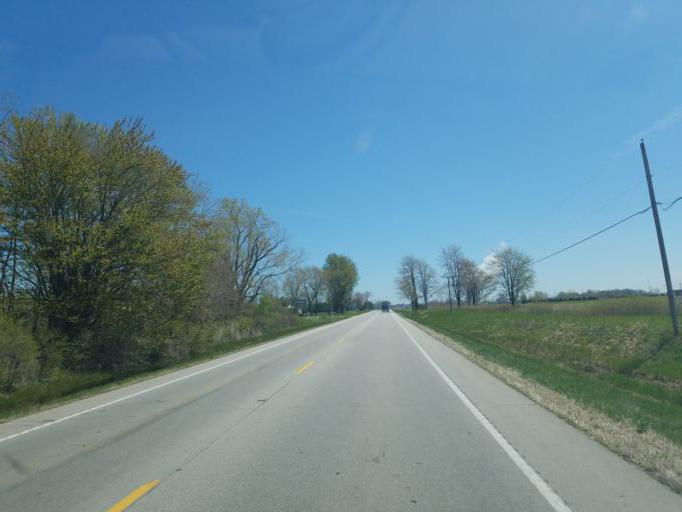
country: US
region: Ohio
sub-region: Ottawa County
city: Oak Harbor
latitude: 41.6039
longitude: -83.1336
